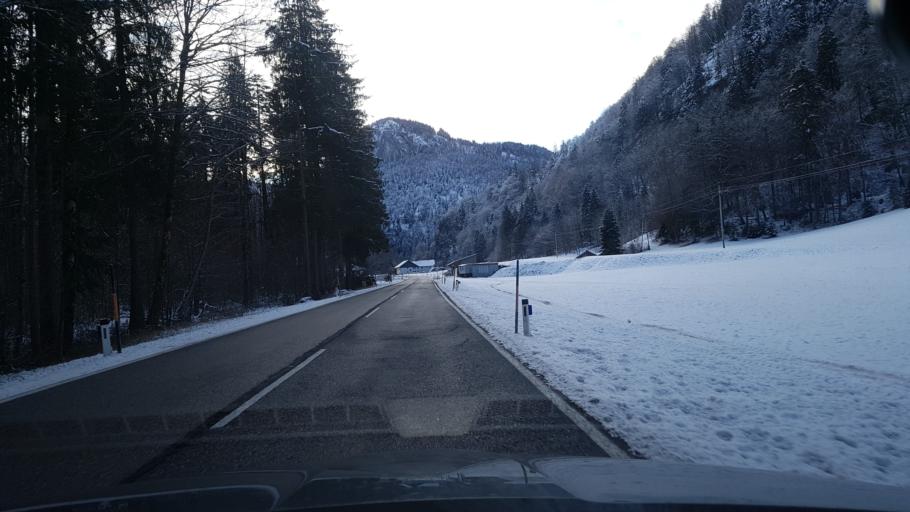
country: AT
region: Salzburg
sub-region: Politischer Bezirk Salzburg-Umgebung
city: Hintersee
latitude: 47.7233
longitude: 13.2778
